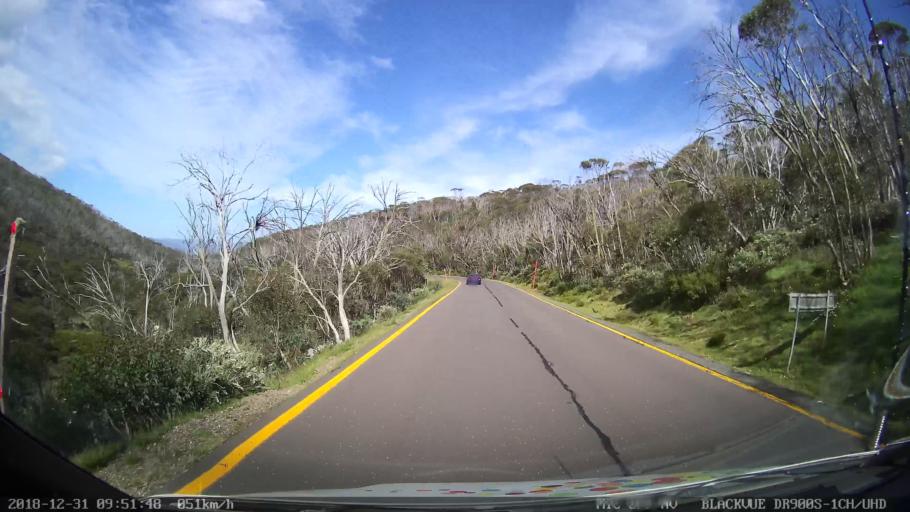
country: AU
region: New South Wales
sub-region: Snowy River
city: Jindabyne
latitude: -36.5243
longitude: 148.2596
